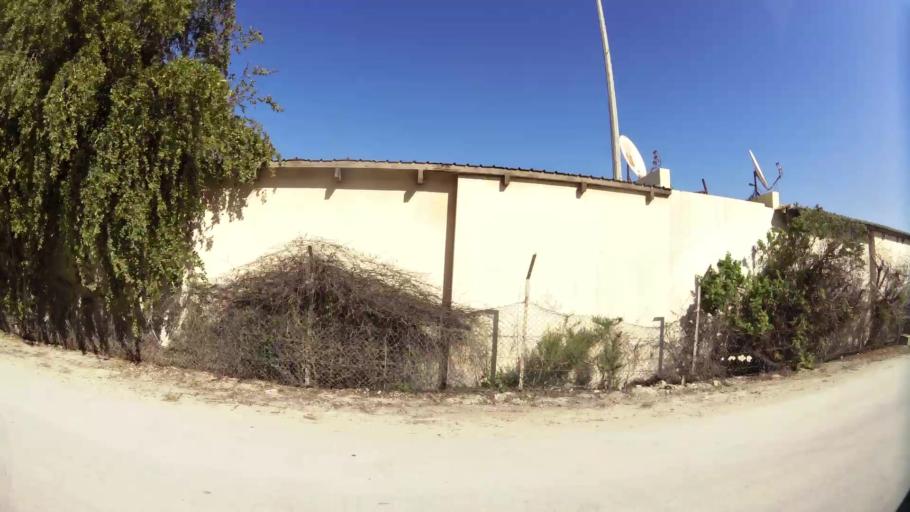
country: BH
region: Manama
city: Manama
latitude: 26.2076
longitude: 50.5714
